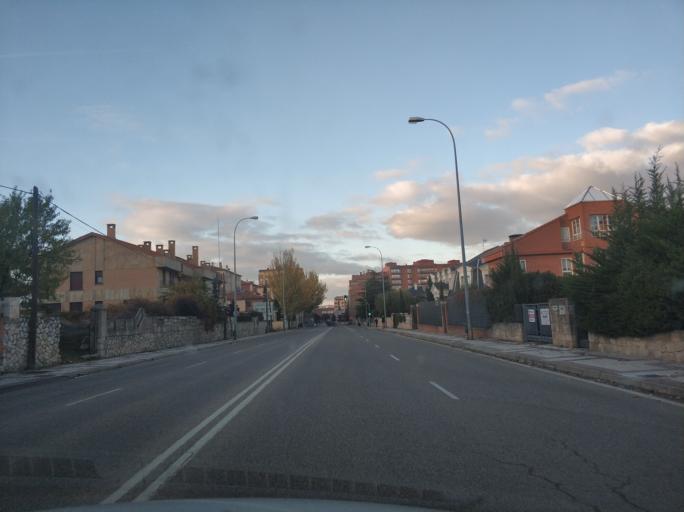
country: ES
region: Castille and Leon
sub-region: Provincia de Soria
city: Soria
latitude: 41.7635
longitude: -2.4787
